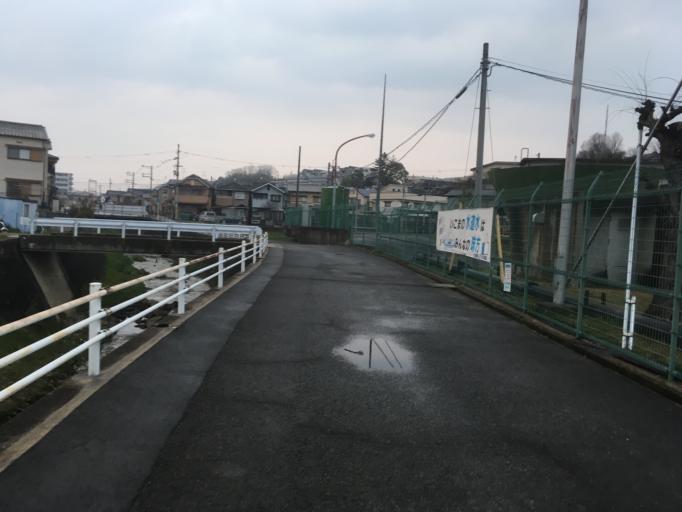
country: JP
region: Nara
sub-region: Ikoma-shi
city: Ikoma
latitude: 34.6887
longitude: 135.7050
